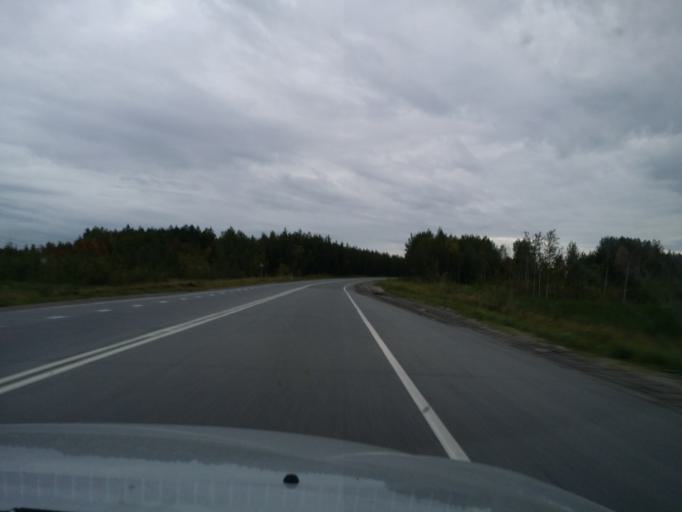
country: RU
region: Khanty-Mansiyskiy Avtonomnyy Okrug
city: Izluchinsk
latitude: 61.0307
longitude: 76.8870
